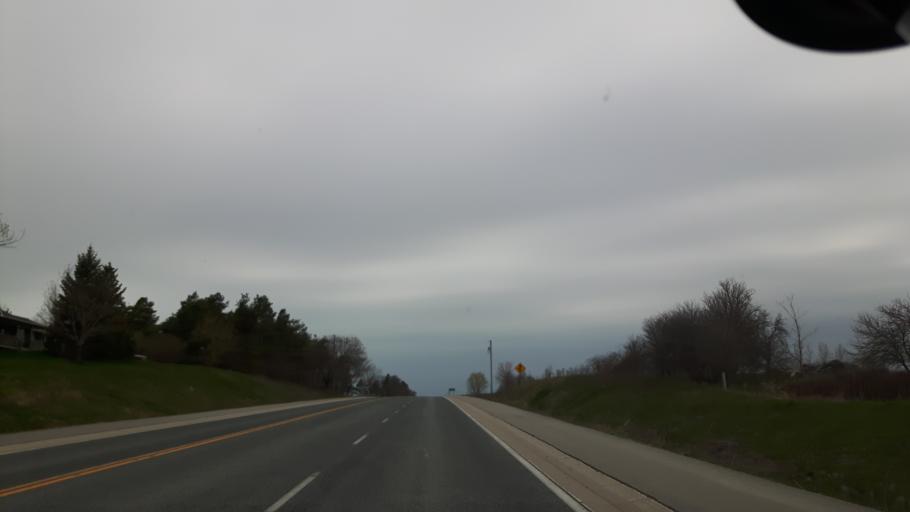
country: CA
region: Ontario
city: Goderich
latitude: 43.6496
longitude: -81.6064
